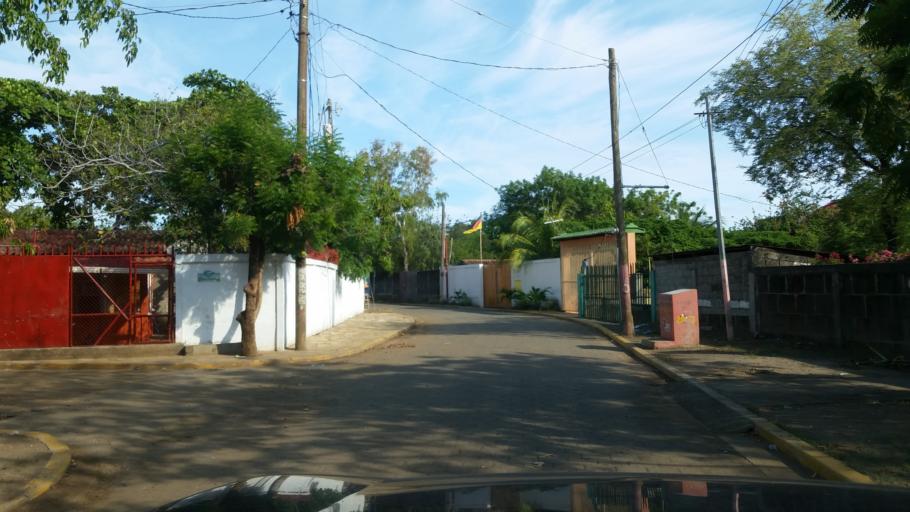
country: NI
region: Managua
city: Masachapa
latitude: 11.7778
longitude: -86.5163
